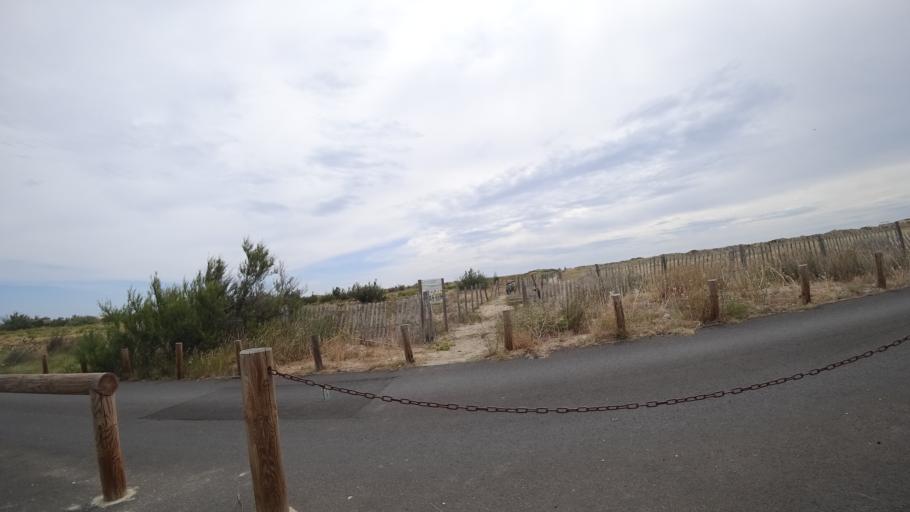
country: FR
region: Languedoc-Roussillon
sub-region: Departement de l'Aude
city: Leucate
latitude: 42.8964
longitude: 3.0516
